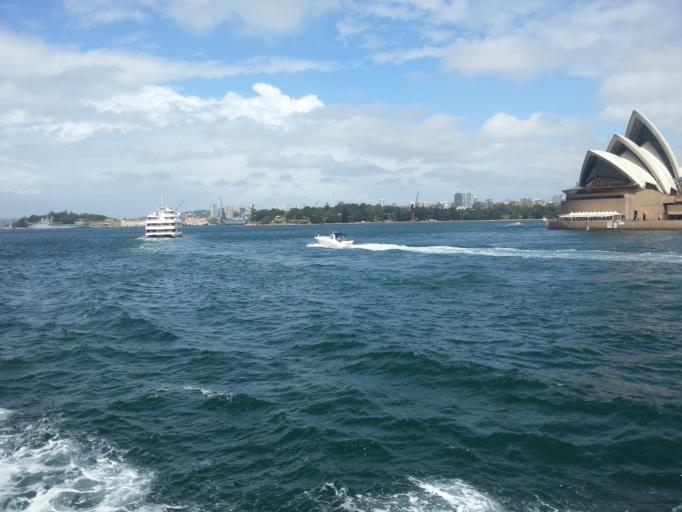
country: AU
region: New South Wales
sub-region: North Sydney
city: Kirribilli
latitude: -33.8539
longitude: 151.2148
